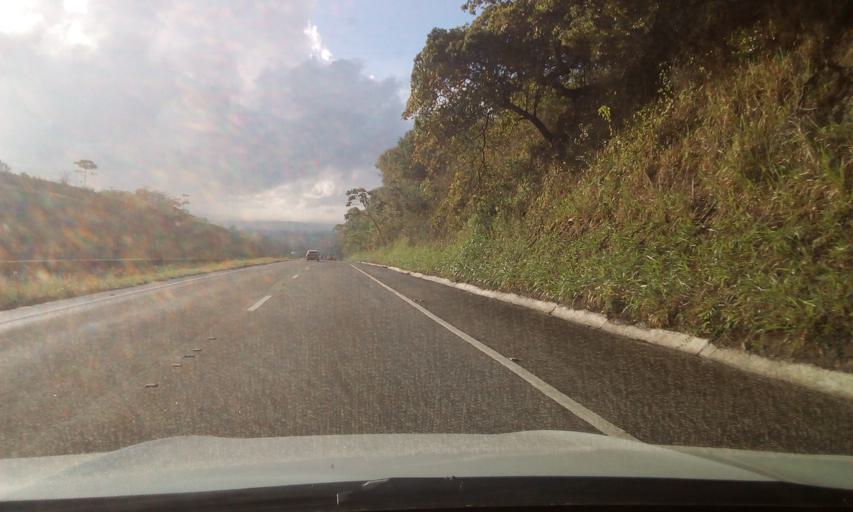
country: BR
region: Pernambuco
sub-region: Itapissuma
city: Itapissuma
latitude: -7.6797
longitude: -34.9265
